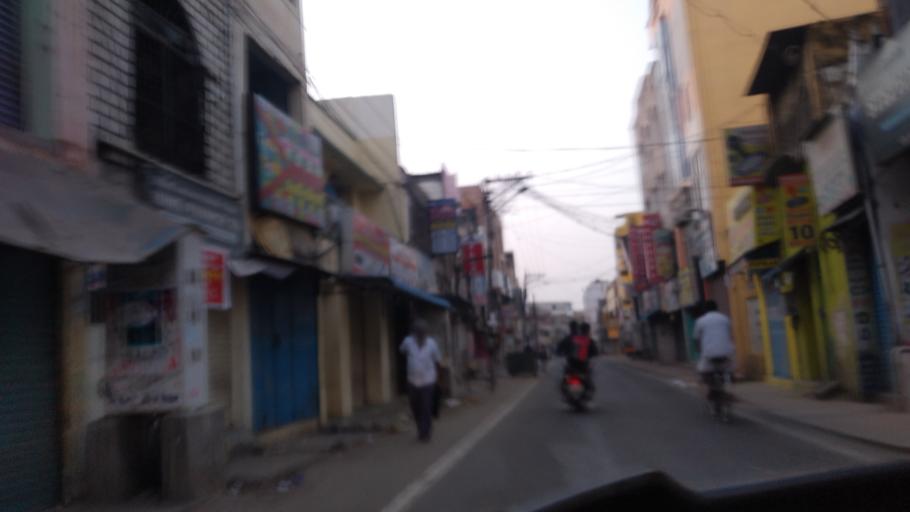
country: IN
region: Tamil Nadu
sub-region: Coimbatore
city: Coimbatore
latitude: 10.9965
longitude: 76.9603
